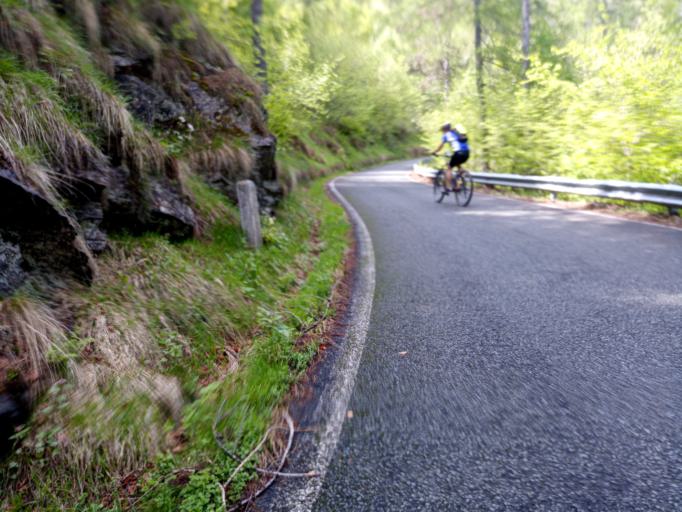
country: IT
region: Piedmont
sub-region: Provincia di Torino
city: Meana di Susa
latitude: 45.1067
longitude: 7.0681
